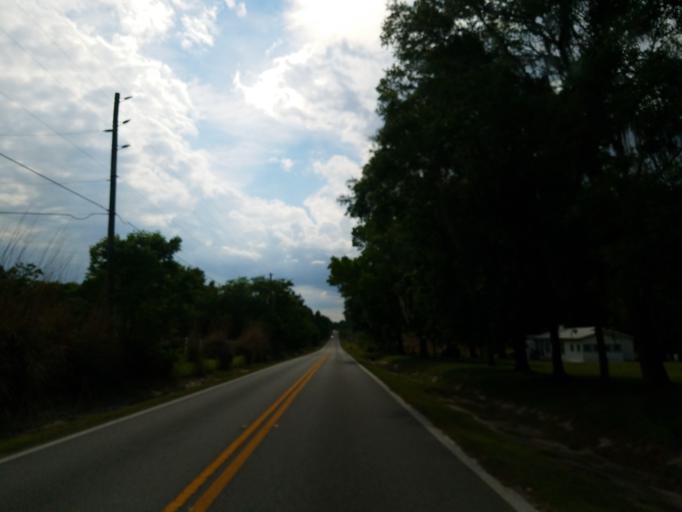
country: US
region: Florida
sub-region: Hernando County
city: Brooksville
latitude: 28.5531
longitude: -82.3375
